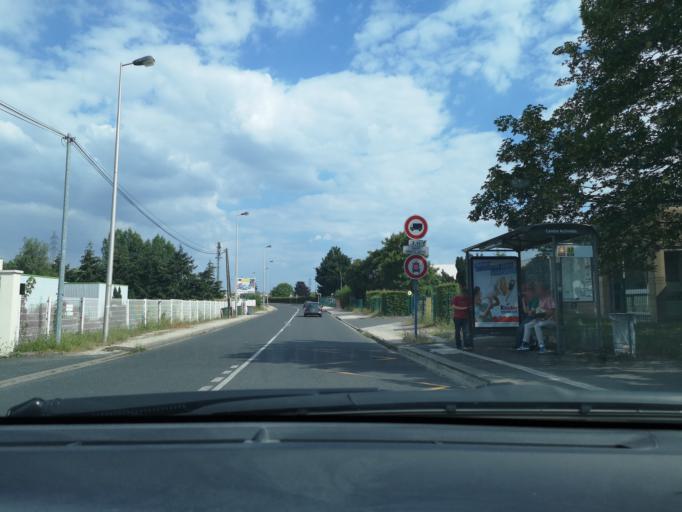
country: FR
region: Centre
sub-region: Departement du Loiret
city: Semoy
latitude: 47.9401
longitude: 1.9346
